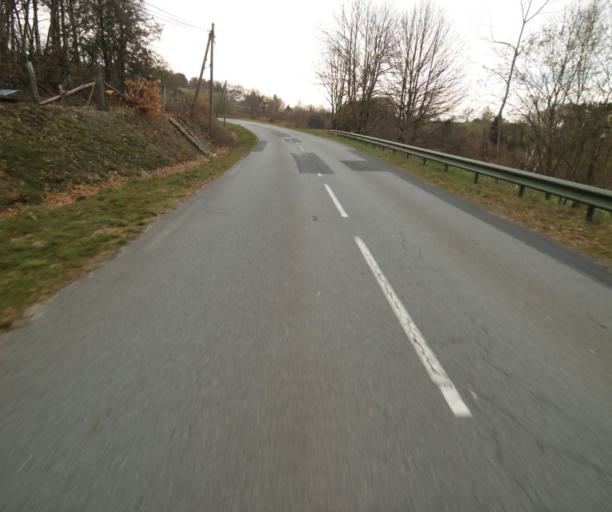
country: FR
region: Limousin
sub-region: Departement de la Correze
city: Correze
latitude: 45.4302
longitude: 1.8280
